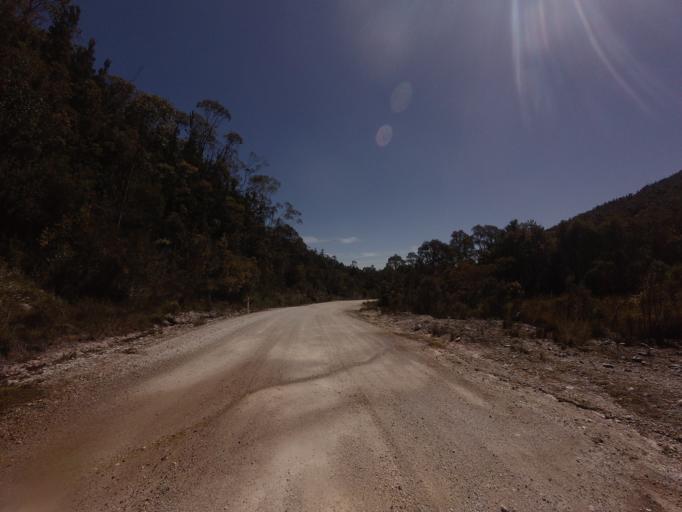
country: AU
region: Tasmania
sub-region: Huon Valley
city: Geeveston
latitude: -42.8193
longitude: 146.3878
